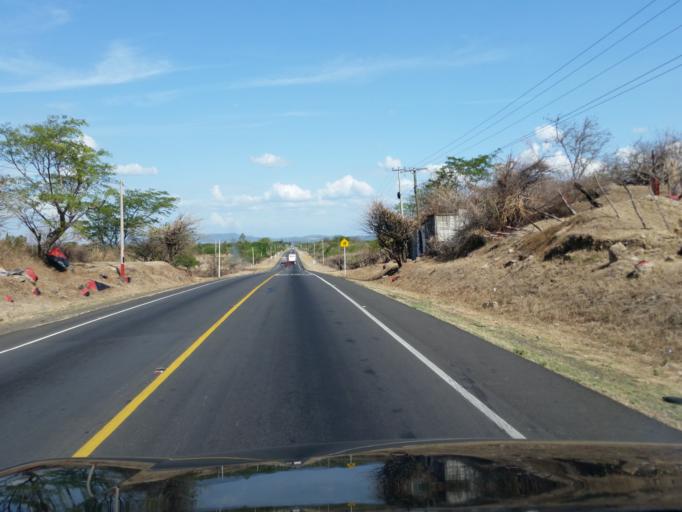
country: NI
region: Leon
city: La Paz Centro
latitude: 12.2982
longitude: -86.7700
